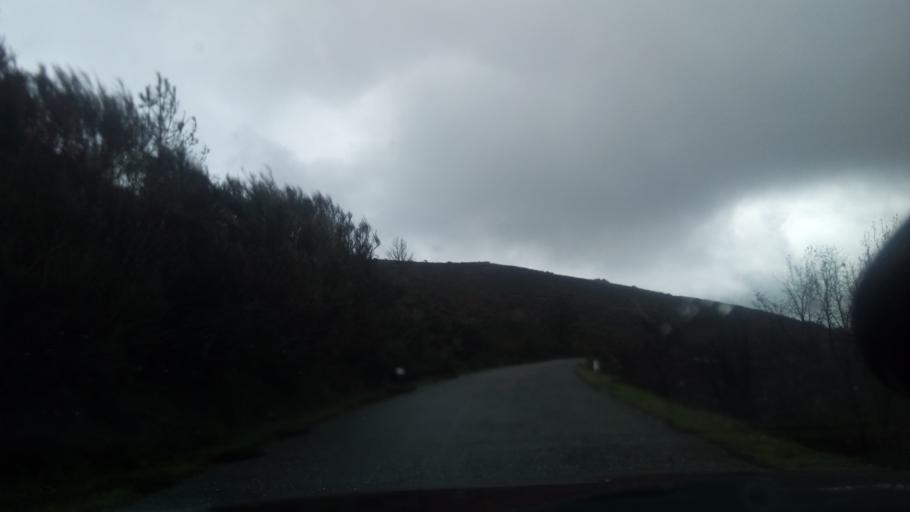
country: PT
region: Guarda
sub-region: Celorico da Beira
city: Celorico da Beira
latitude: 40.5382
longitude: -7.4450
